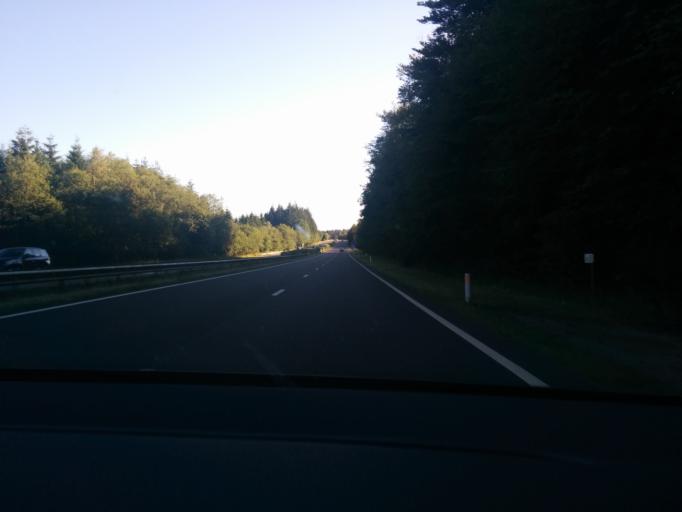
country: BE
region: Wallonia
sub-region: Province du Luxembourg
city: Saint-Hubert
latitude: 50.0568
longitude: 5.4059
